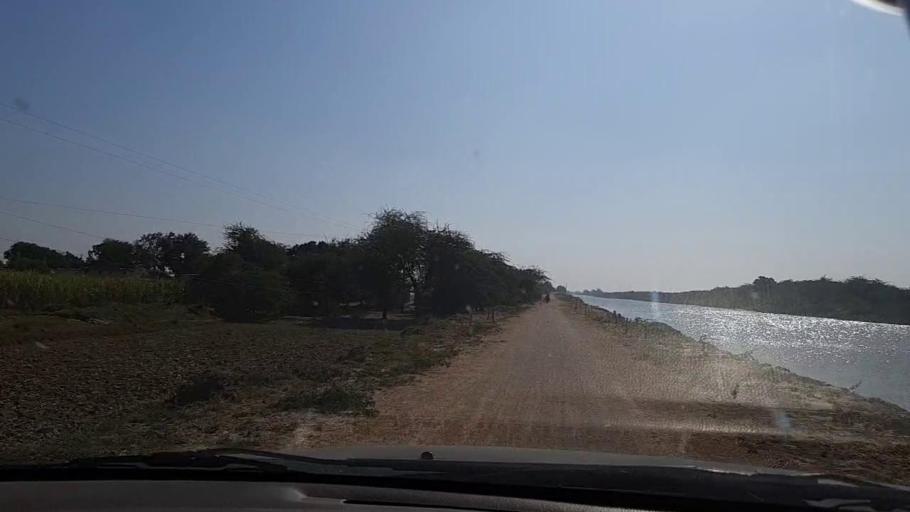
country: PK
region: Sindh
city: Thatta
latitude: 24.6025
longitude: 68.0507
